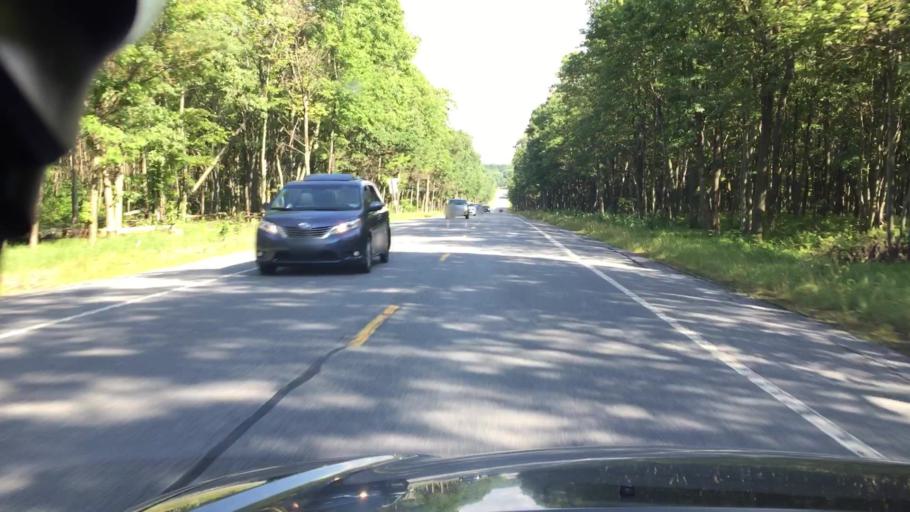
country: US
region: Pennsylvania
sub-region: Carbon County
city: Nesquehoning
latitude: 40.8986
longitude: -75.8148
